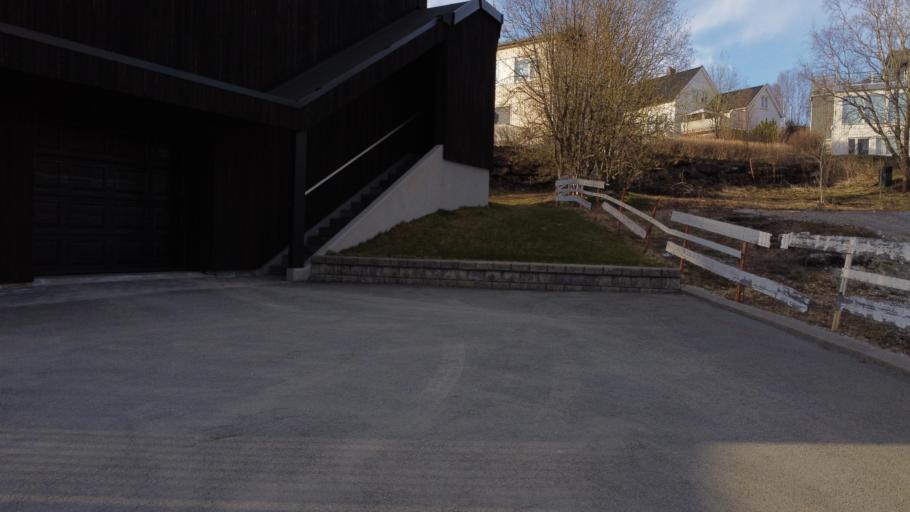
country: NO
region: Nordland
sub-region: Rana
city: Mo i Rana
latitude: 66.3140
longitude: 14.1372
